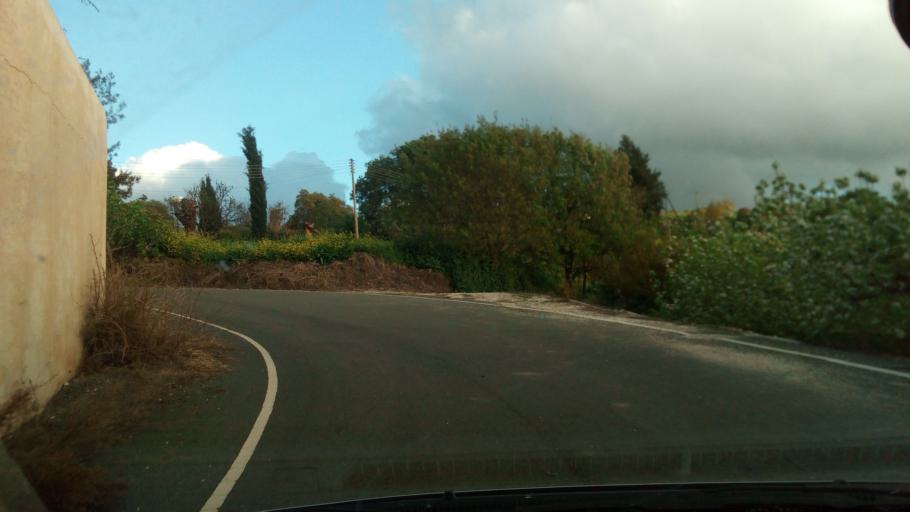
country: CY
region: Pafos
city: Polis
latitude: 34.9974
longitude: 32.5084
